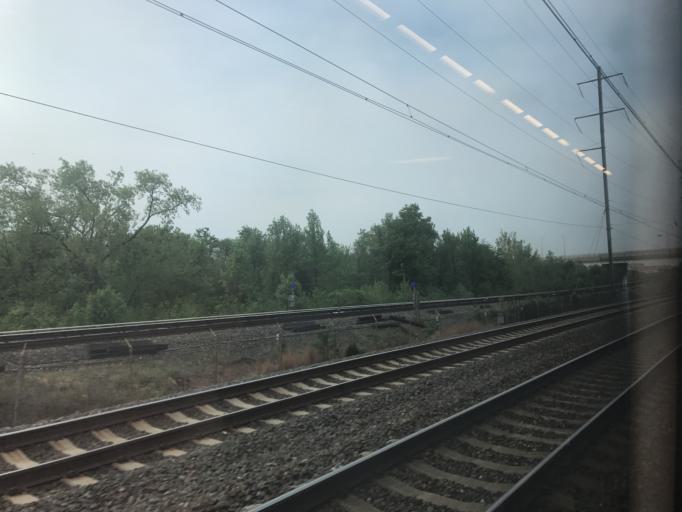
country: US
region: Maryland
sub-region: Prince George's County
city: Landover Hills
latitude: 38.9432
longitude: -76.8779
